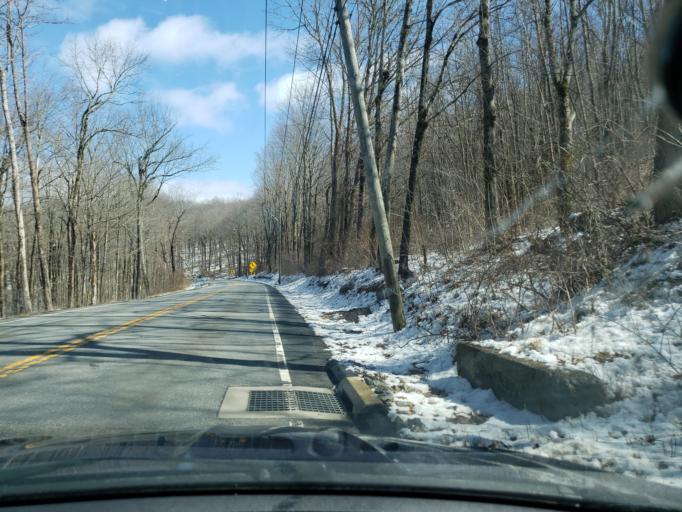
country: US
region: Connecticut
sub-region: Litchfield County
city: New Preston
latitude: 41.7150
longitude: -73.3211
